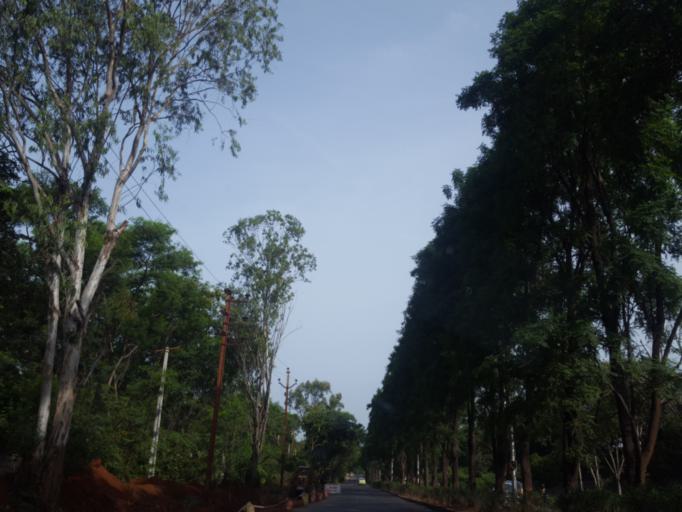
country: IN
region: Telangana
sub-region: Medak
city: Serilingampalle
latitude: 17.4545
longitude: 78.3421
